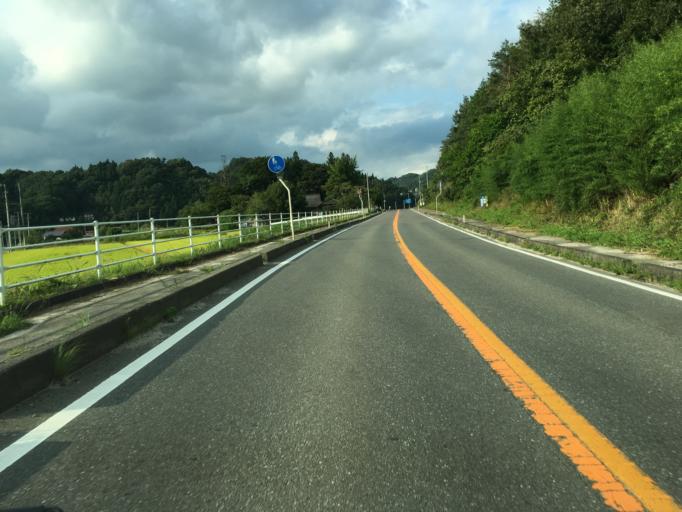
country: JP
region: Fukushima
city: Hobaramachi
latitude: 37.7014
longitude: 140.6069
